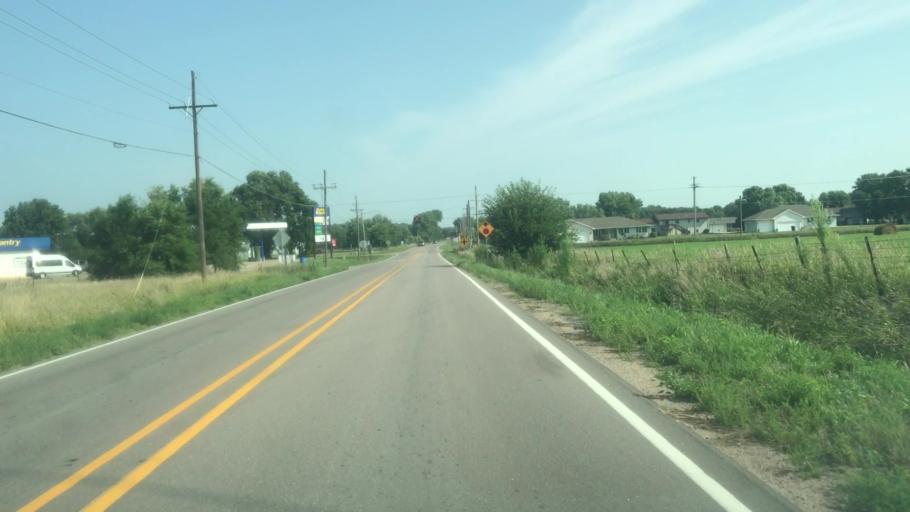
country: US
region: Nebraska
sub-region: Hall County
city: Grand Island
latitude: 40.9144
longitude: -98.3018
